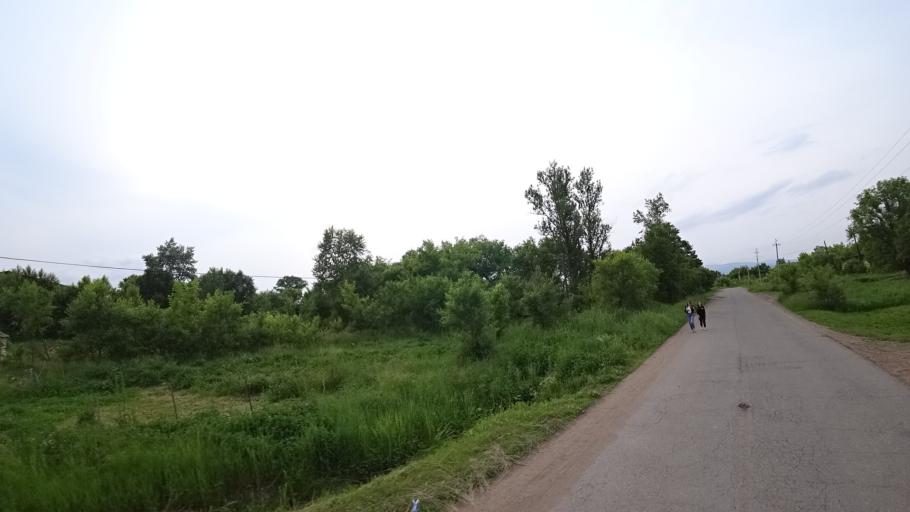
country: RU
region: Primorskiy
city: Novosysoyevka
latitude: 44.2425
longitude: 133.3676
